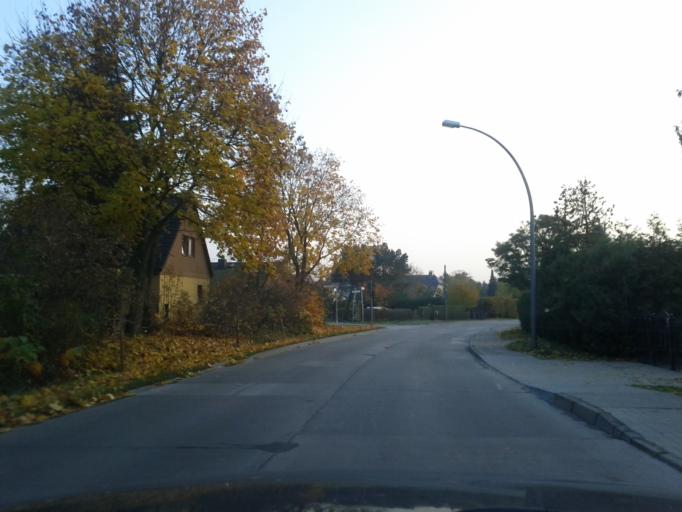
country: DE
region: Berlin
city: Mahlsdorf
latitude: 52.4982
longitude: 13.6205
